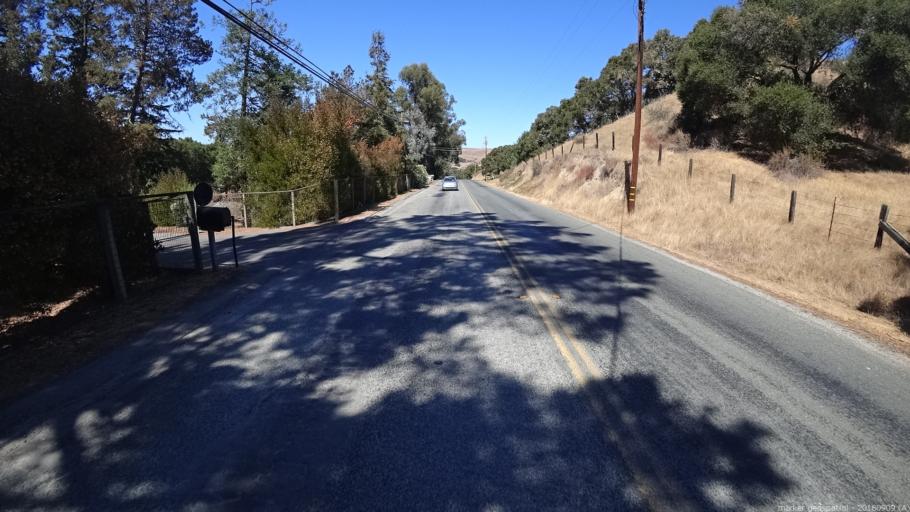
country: US
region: California
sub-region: Monterey County
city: Carmel Valley Village
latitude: 36.5731
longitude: -121.7119
